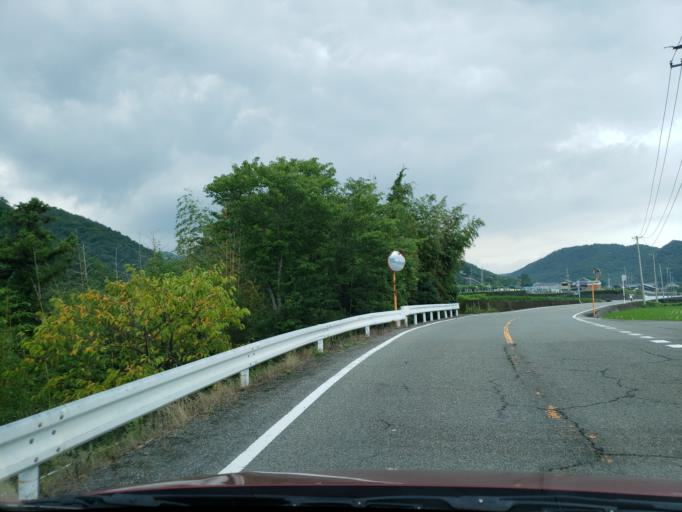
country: JP
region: Tokushima
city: Kamojimacho-jogejima
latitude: 34.1076
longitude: 134.2802
